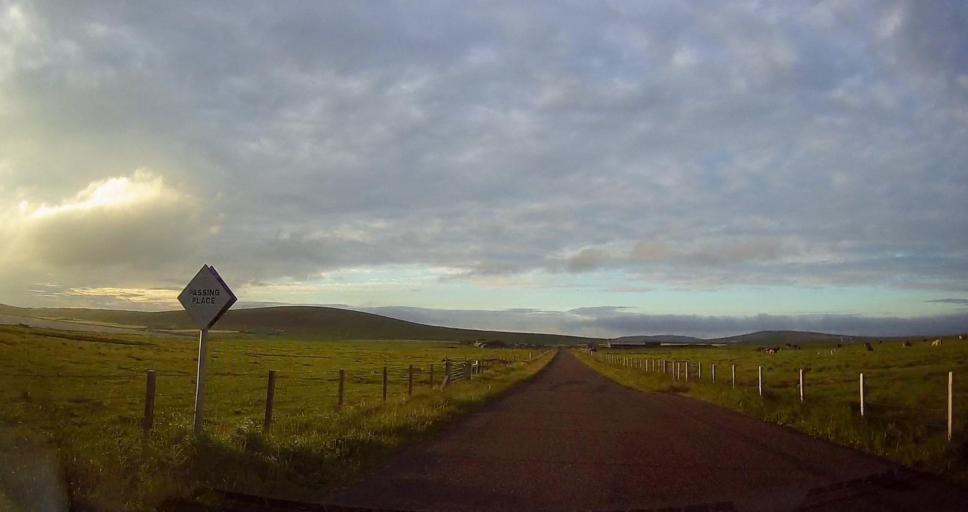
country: GB
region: Scotland
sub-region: Orkney Islands
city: Stromness
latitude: 59.1048
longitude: -3.2565
